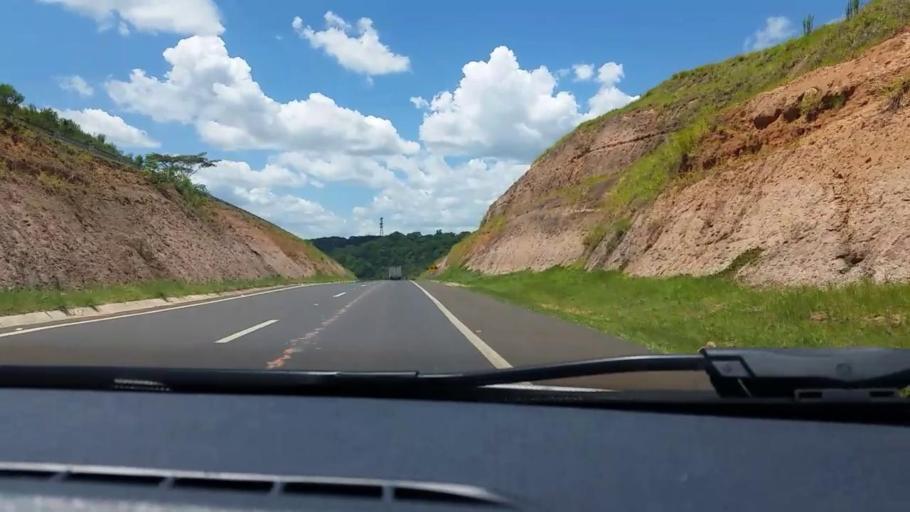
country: BR
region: Sao Paulo
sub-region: Bauru
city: Bauru
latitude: -22.4377
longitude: -49.1397
